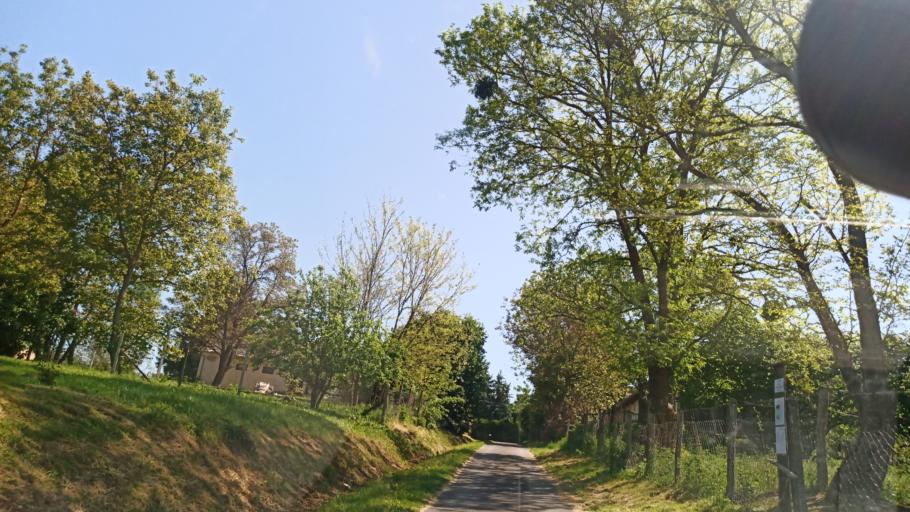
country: HU
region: Zala
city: Pacsa
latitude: 46.6242
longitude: 17.0448
